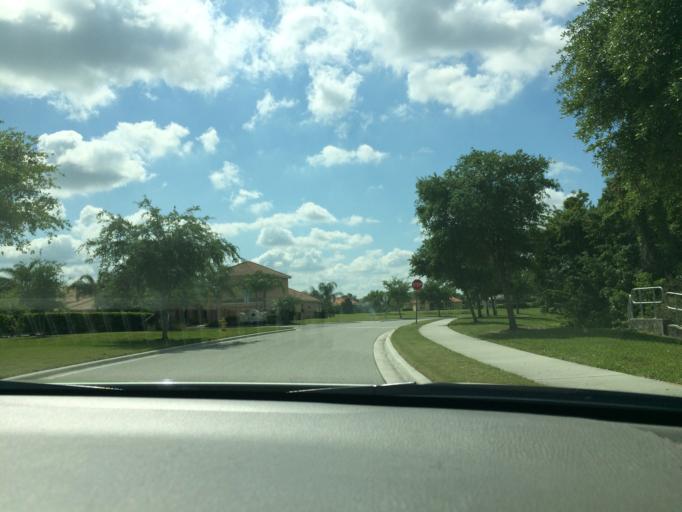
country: US
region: Florida
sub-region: Manatee County
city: Ellenton
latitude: 27.5093
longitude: -82.4200
